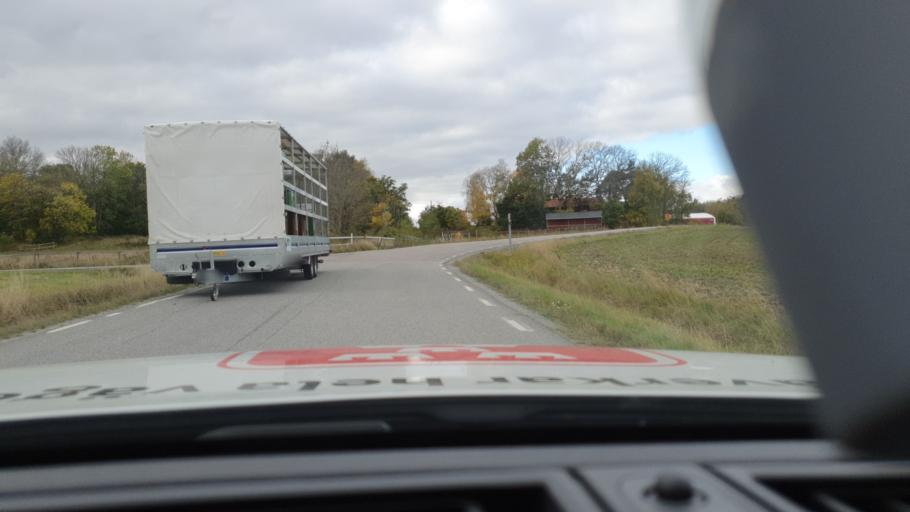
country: SE
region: Stockholm
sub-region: Upplands-Bro Kommun
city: Bro
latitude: 59.5071
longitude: 17.5852
